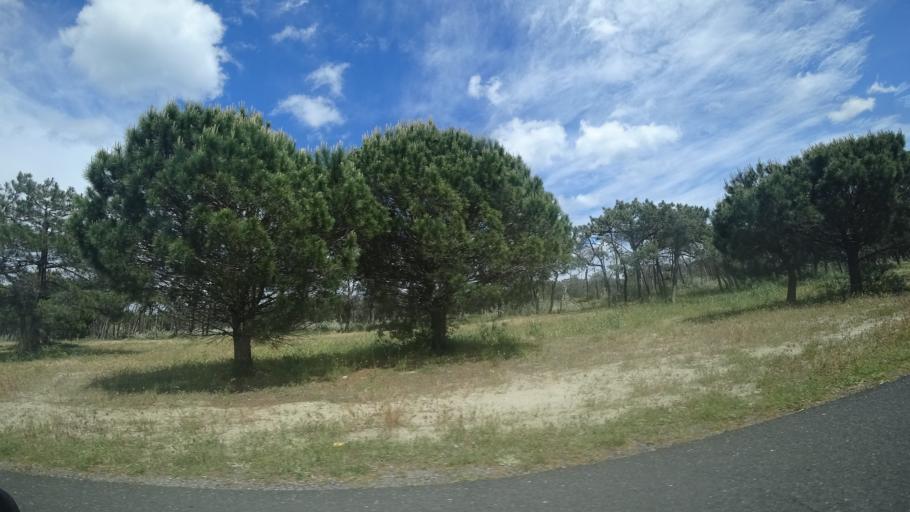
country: FR
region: Languedoc-Roussillon
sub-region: Departement des Pyrenees-Orientales
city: Le Barcares
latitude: 42.8132
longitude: 3.0308
